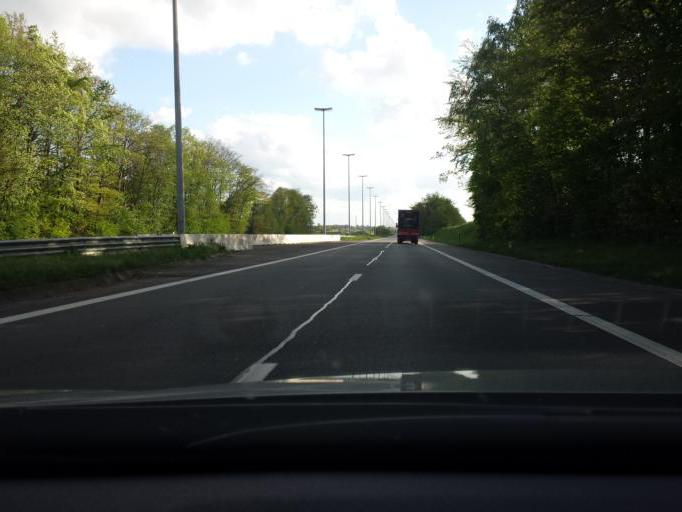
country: BE
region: Wallonia
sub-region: Province de Liege
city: Lontzen
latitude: 50.6837
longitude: 6.0504
